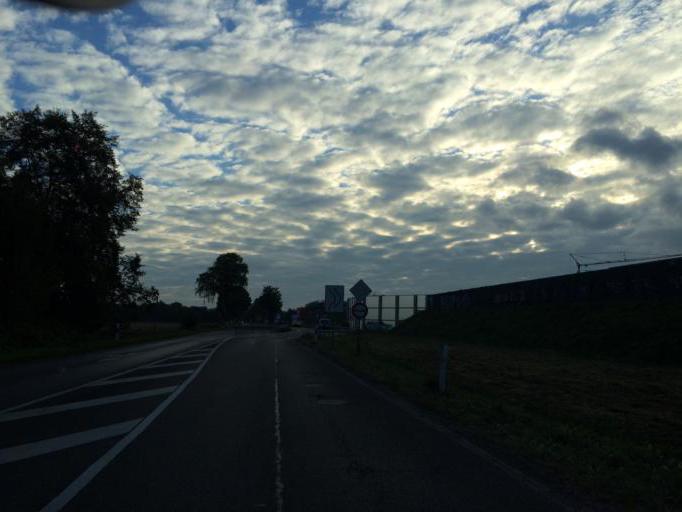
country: DE
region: North Rhine-Westphalia
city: Sankt Augustin
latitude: 50.7522
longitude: 7.1498
